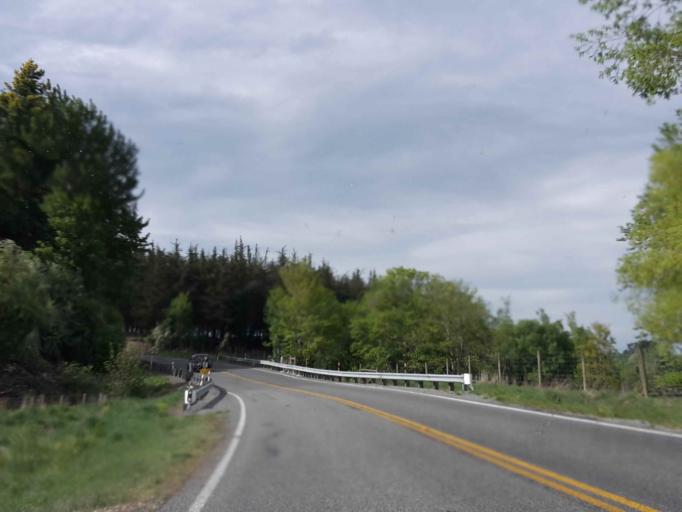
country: NZ
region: Canterbury
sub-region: Timaru District
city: Pleasant Point
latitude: -44.1163
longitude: 171.1337
